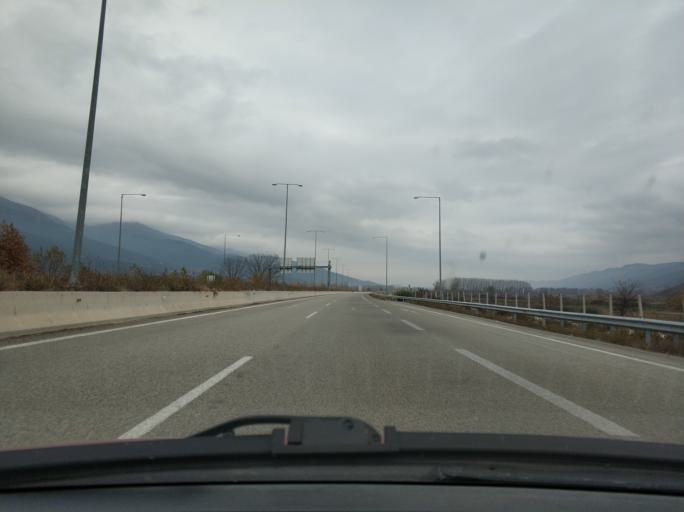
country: GR
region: East Macedonia and Thrace
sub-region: Nomos Kavalas
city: Nikisiani
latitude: 40.8413
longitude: 24.1182
